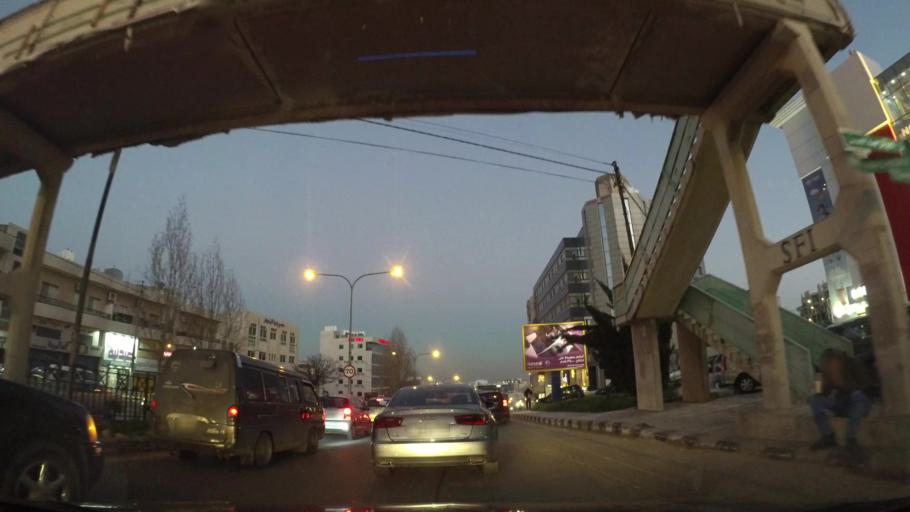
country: JO
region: Amman
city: Al Jubayhah
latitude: 31.9966
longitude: 35.8537
